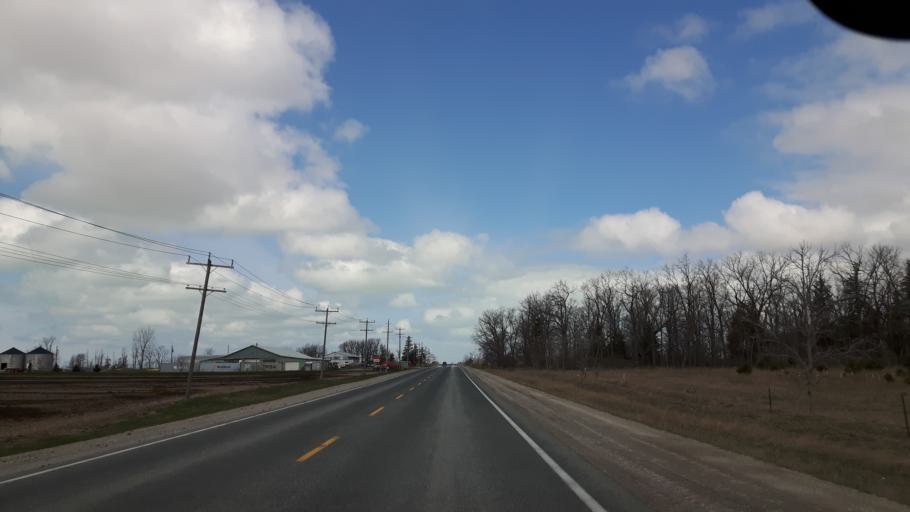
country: CA
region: Ontario
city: Goderich
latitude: 43.7165
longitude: -81.6691
